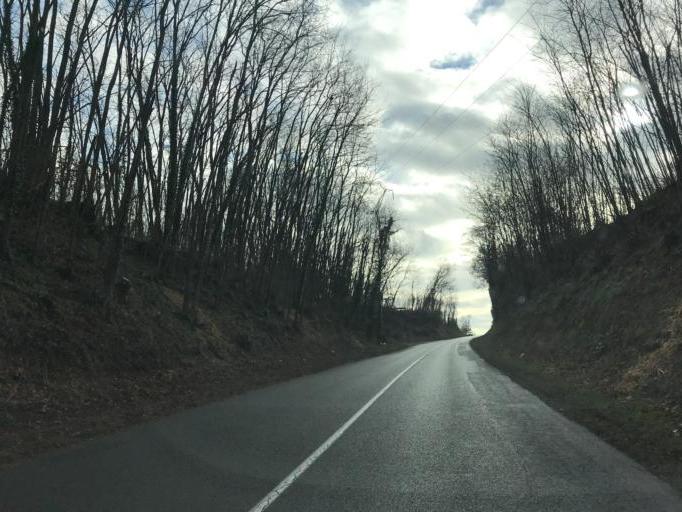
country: FR
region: Rhone-Alpes
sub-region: Departement de l'Ain
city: Sainte-Euphemie
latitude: 45.9623
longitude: 4.7995
